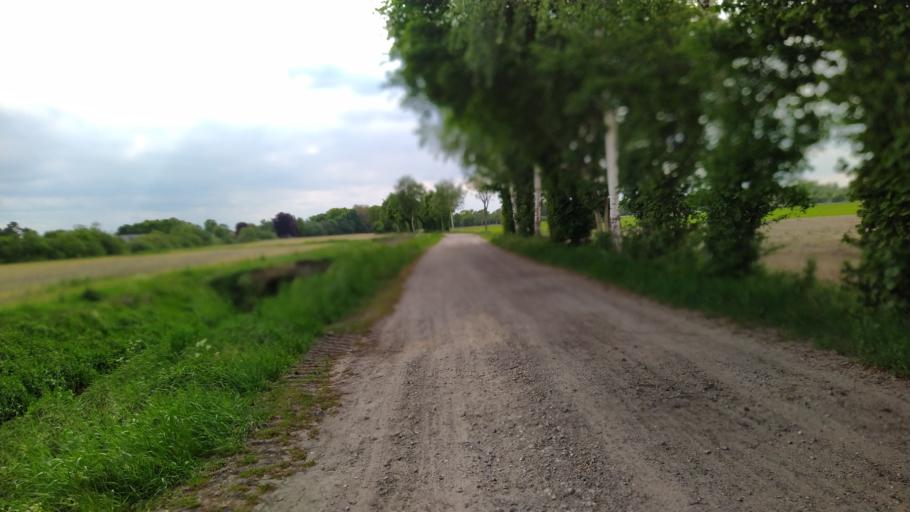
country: DE
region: Lower Saxony
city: Grasberg
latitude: 53.1957
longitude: 9.0276
